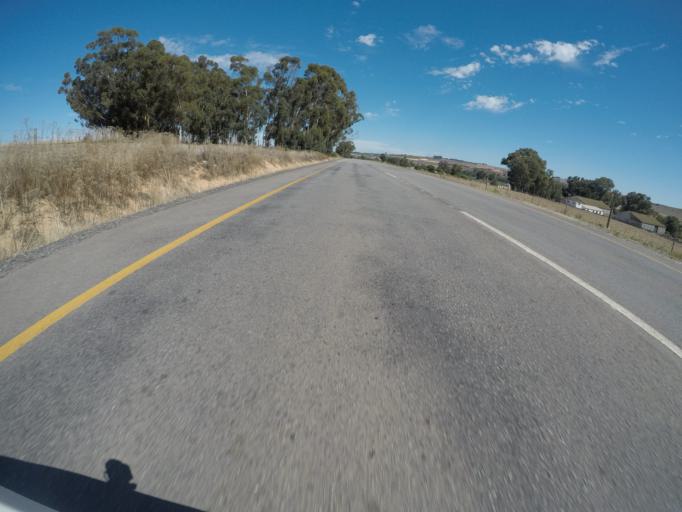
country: ZA
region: Western Cape
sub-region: West Coast District Municipality
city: Malmesbury
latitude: -33.4824
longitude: 18.6970
